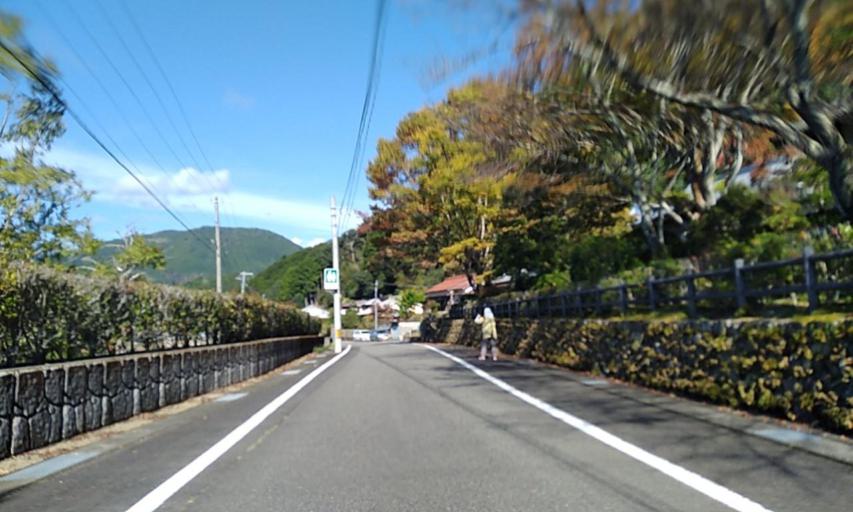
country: JP
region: Wakayama
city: Shingu
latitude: 33.9254
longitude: 135.9831
